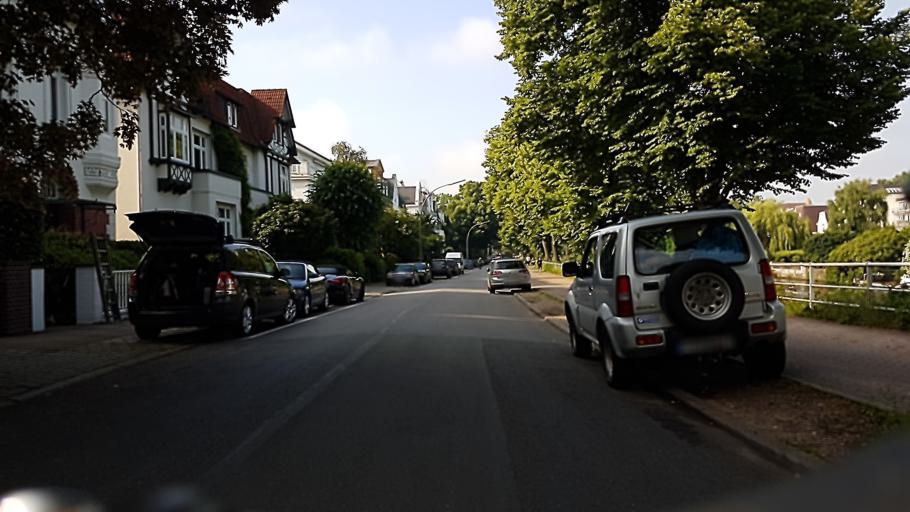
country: DE
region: Hamburg
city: Winterhude
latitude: 53.5878
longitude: 9.9977
